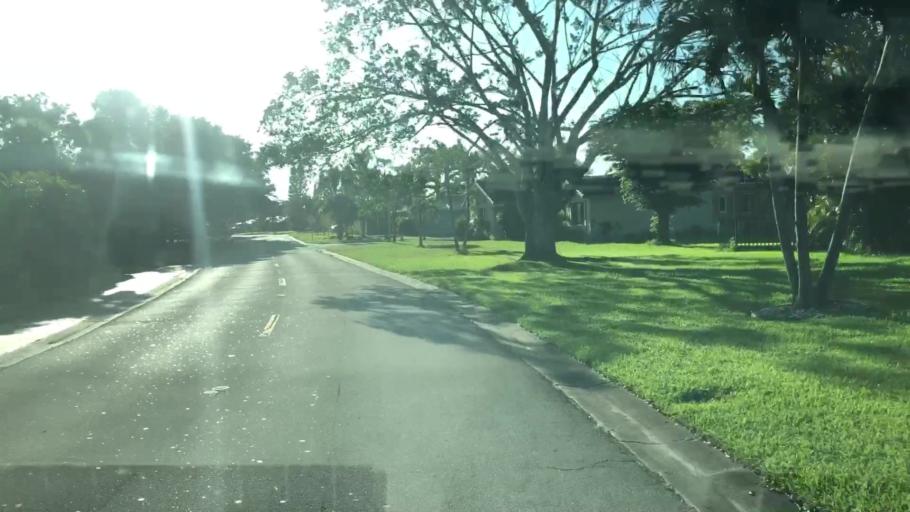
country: US
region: Florida
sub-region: Broward County
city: Coral Springs
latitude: 26.2774
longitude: -80.2637
